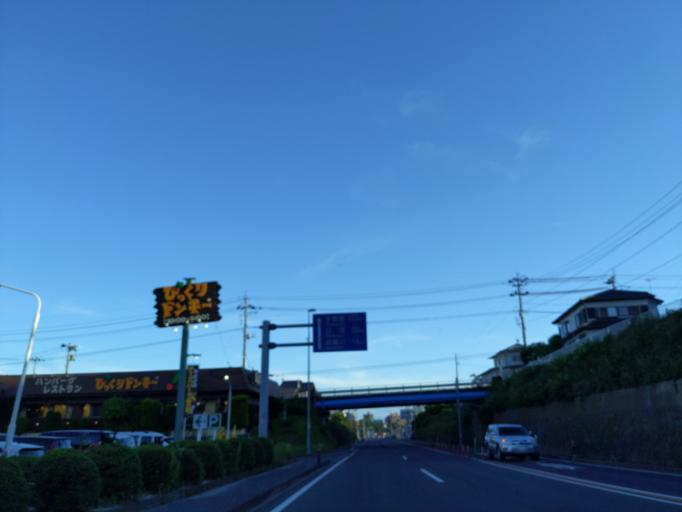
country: JP
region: Fukushima
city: Koriyama
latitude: 37.4120
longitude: 140.3862
